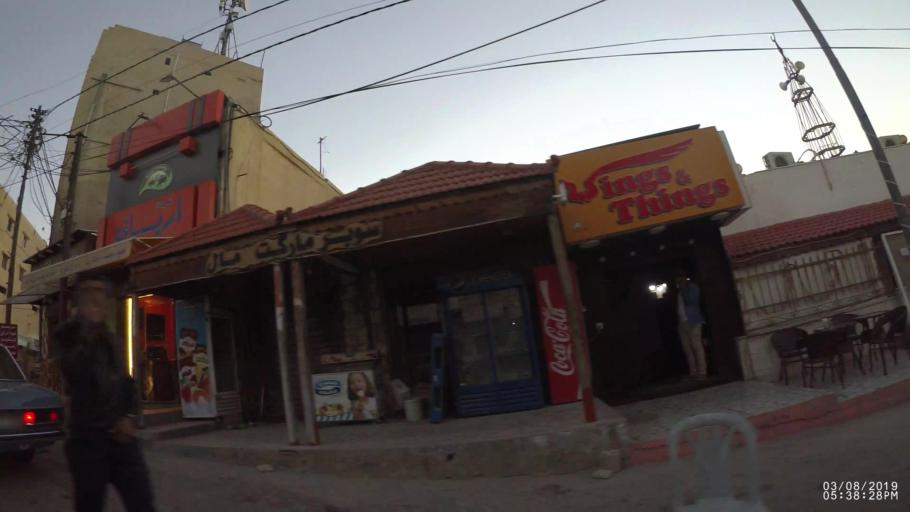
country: JO
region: Ma'an
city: Petra
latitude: 30.3210
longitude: 35.4789
